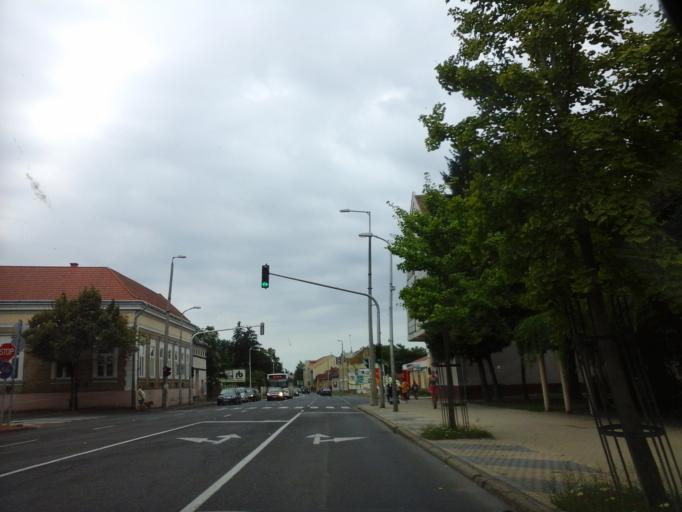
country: HU
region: Hajdu-Bihar
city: Hajduszoboszlo
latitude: 47.4431
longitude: 21.3886
